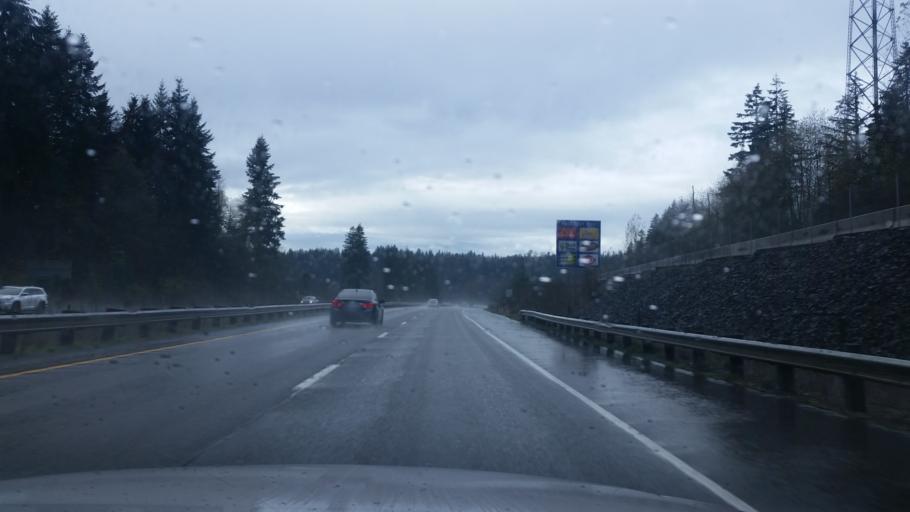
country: US
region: Washington
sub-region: King County
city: Maple Valley
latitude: 47.4102
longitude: -122.0309
